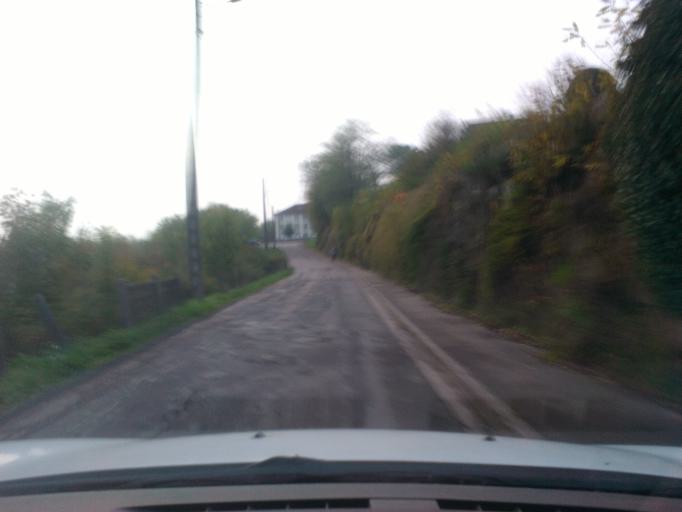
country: FR
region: Lorraine
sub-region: Departement des Vosges
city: Mirecourt
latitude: 48.3003
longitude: 6.1281
